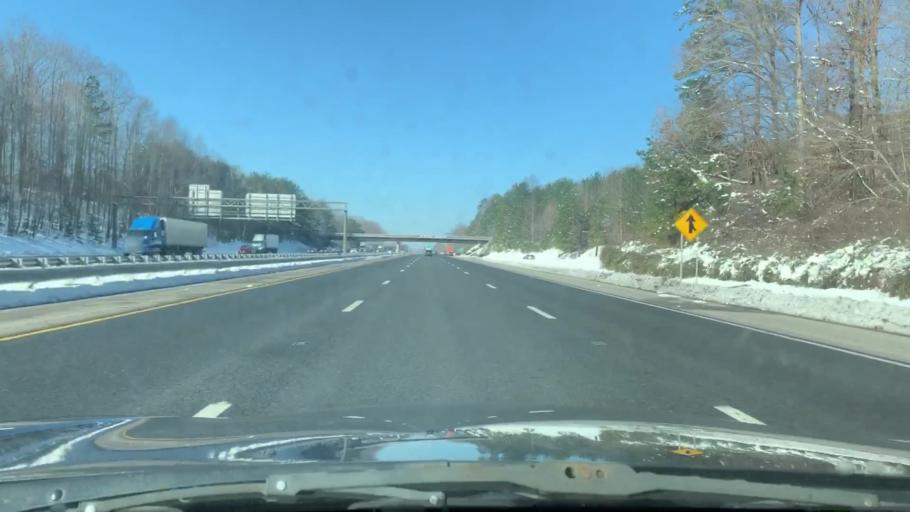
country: US
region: North Carolina
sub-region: Orange County
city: Hillsborough
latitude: 36.0603
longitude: -79.1321
